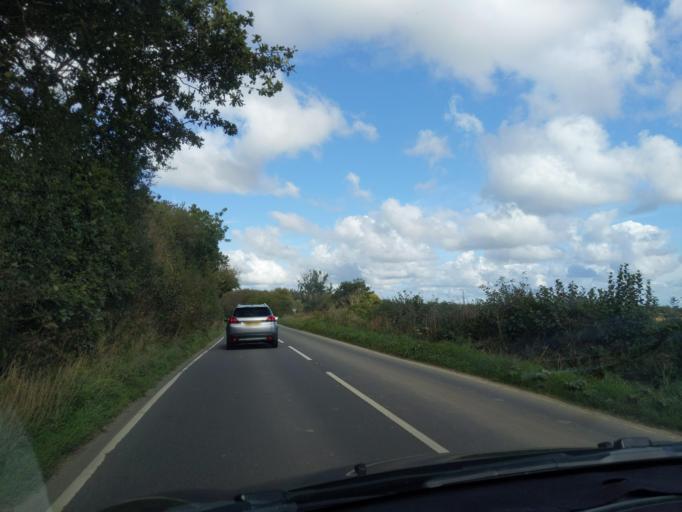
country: GB
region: England
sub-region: Devon
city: Holsworthy
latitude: 50.8599
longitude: -4.3258
